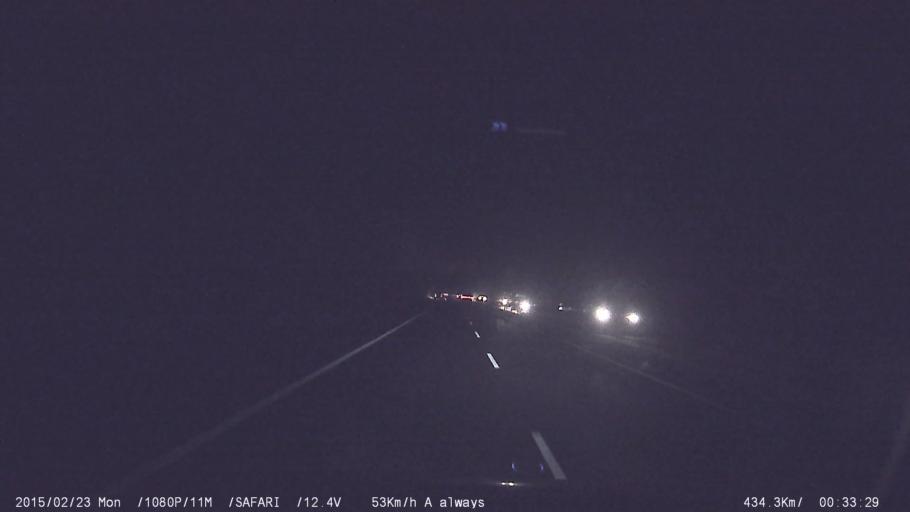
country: IN
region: Tamil Nadu
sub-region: Dharmapuri
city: Dharmapuri
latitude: 11.9739
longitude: 78.0529
